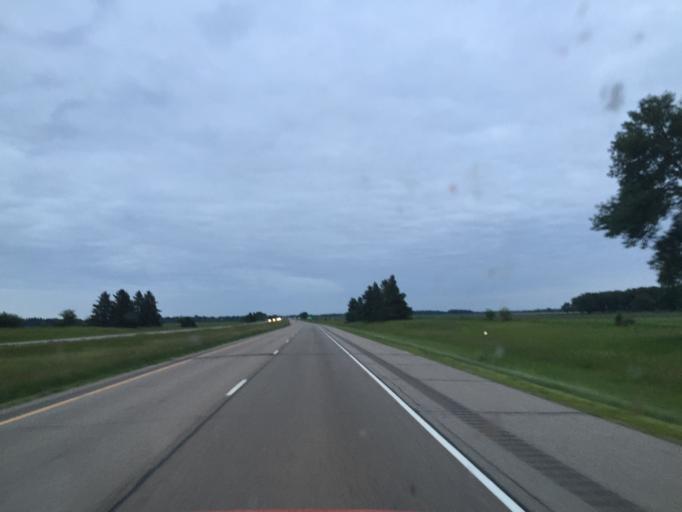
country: US
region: Minnesota
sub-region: Mower County
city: Austin
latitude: 43.6596
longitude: -93.0616
